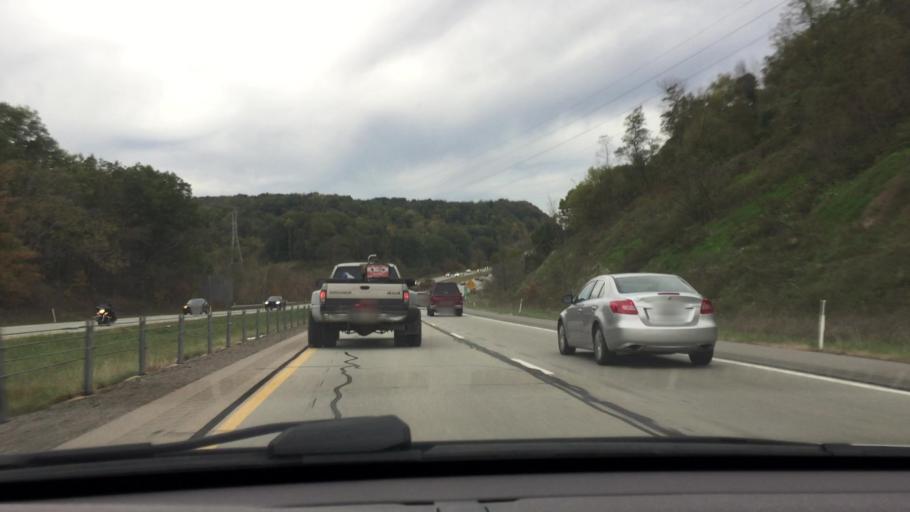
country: US
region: Pennsylvania
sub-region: Beaver County
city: Ambridge
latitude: 40.5762
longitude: -80.2877
